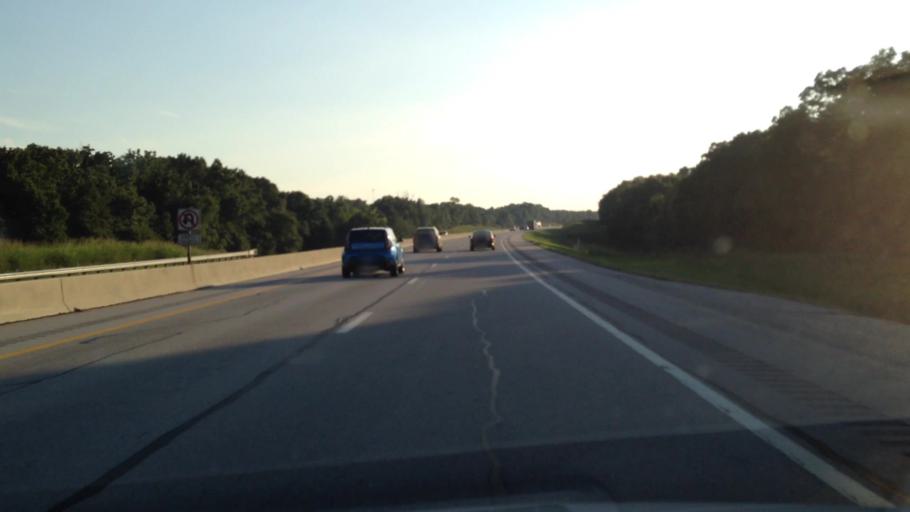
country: US
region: Kansas
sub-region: Cherokee County
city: Baxter Springs
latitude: 36.9432
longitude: -94.6858
